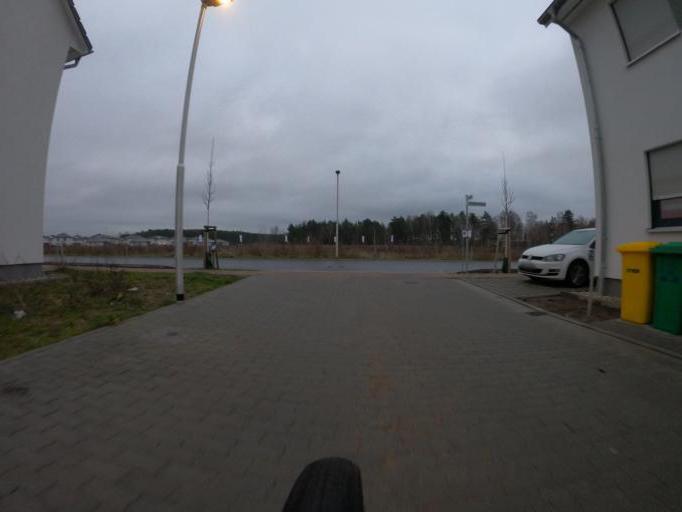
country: DE
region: Brandenburg
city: Schulzendorf
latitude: 52.3567
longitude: 13.5802
